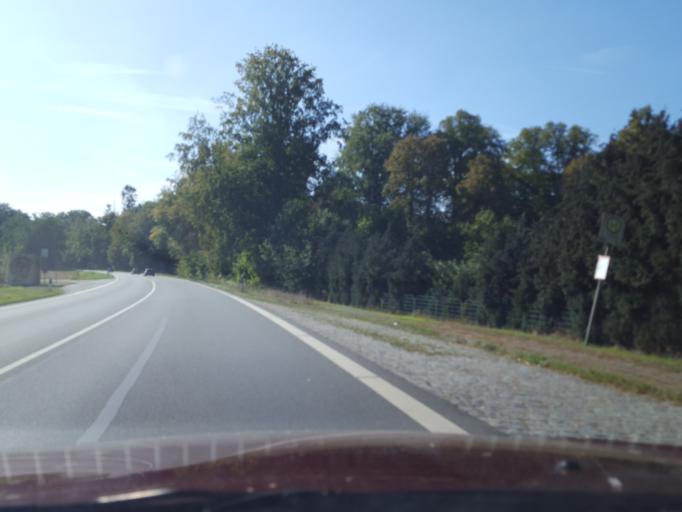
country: DE
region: Lower Saxony
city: Eystrup
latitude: 52.8172
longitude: 9.1987
